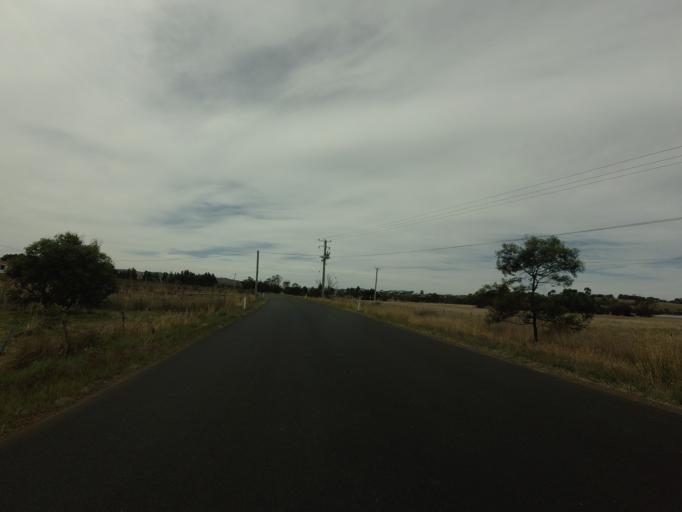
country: AU
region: Tasmania
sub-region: Sorell
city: Sorell
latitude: -42.7814
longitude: 147.5150
